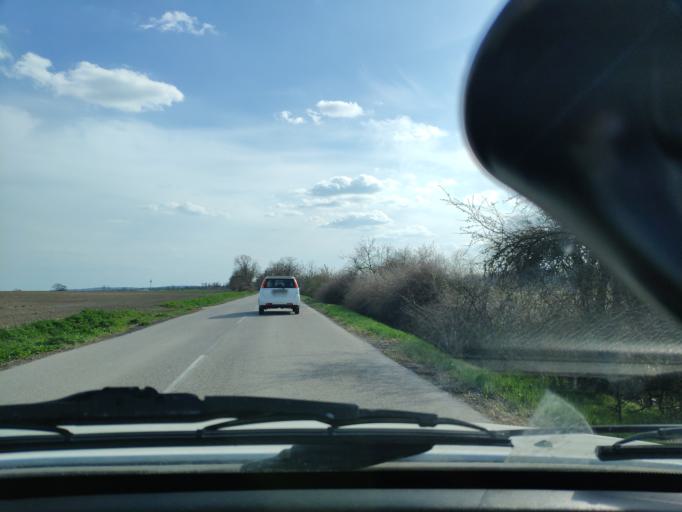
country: HU
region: Fejer
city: Adony
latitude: 47.1289
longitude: 18.8974
